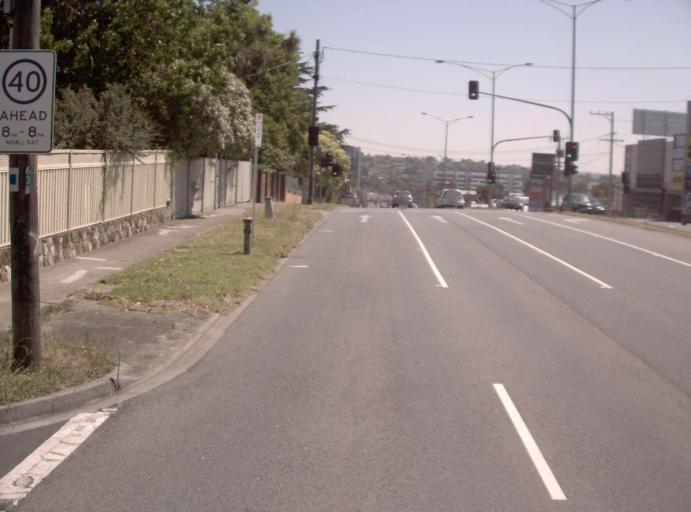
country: AU
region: Victoria
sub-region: Monash
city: Chadstone
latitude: -37.8783
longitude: 145.0910
